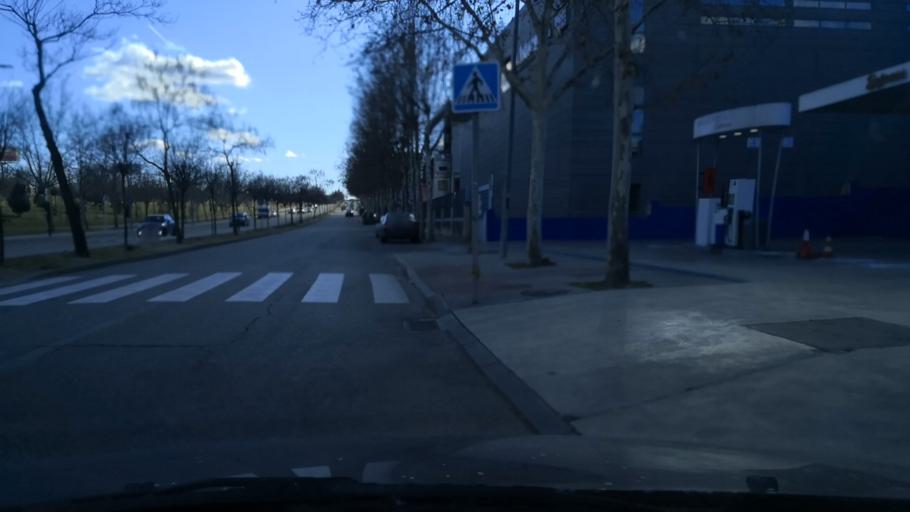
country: ES
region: Madrid
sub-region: Provincia de Madrid
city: San Sebastian de los Reyes
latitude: 40.5521
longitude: -3.6100
